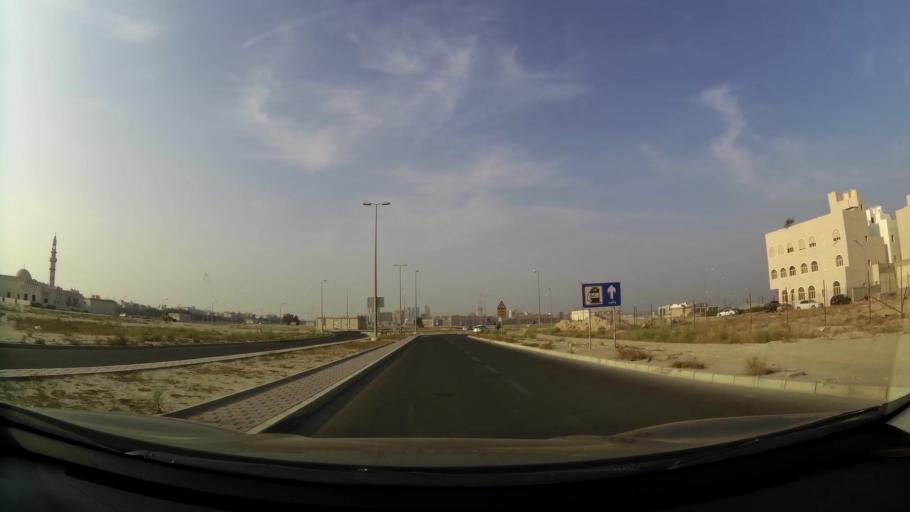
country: KW
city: Al Funaytis
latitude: 29.2363
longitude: 48.0877
